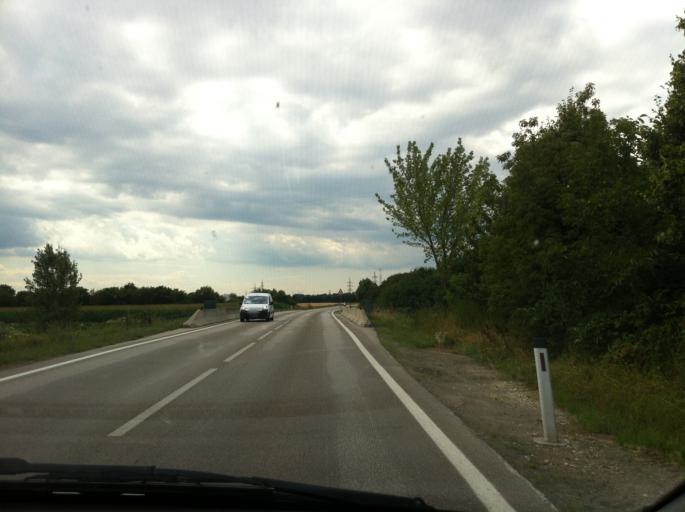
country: AT
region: Lower Austria
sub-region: Politischer Bezirk Tulln
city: Tulln
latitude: 48.3148
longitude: 16.0523
